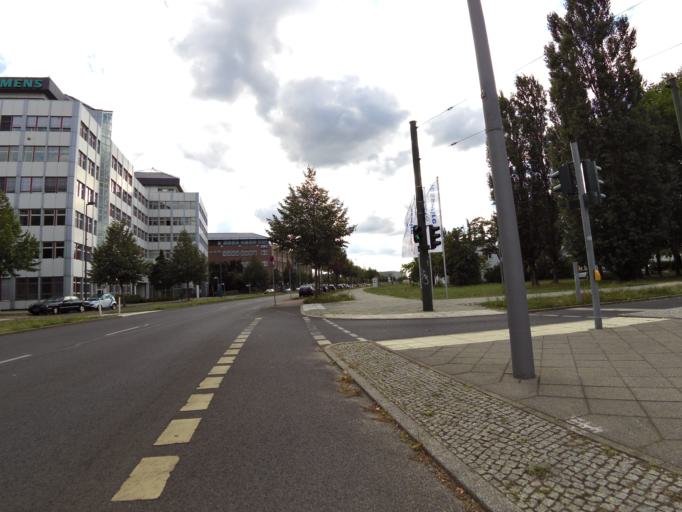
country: DE
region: Berlin
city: Altglienicke
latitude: 52.4295
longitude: 13.5294
